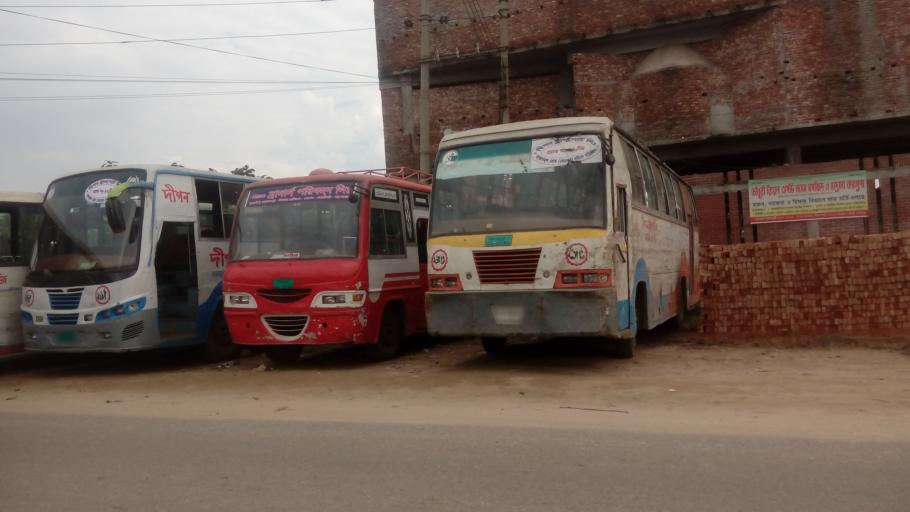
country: BD
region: Dhaka
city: Azimpur
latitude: 23.7527
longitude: 90.3546
